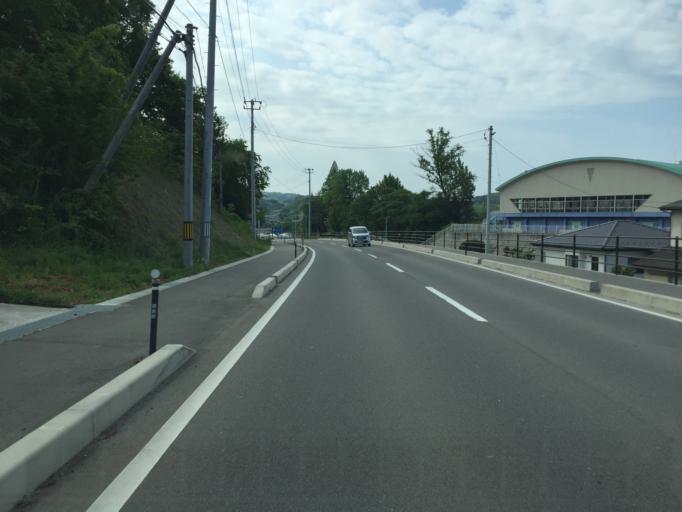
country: JP
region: Fukushima
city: Fukushima-shi
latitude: 37.6606
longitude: 140.5321
